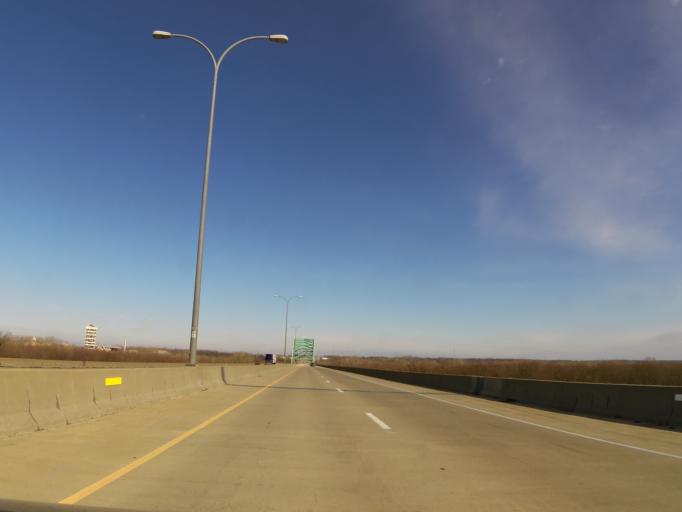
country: US
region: Illinois
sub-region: LaSalle County
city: La Salle
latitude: 41.3186
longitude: -89.0796
